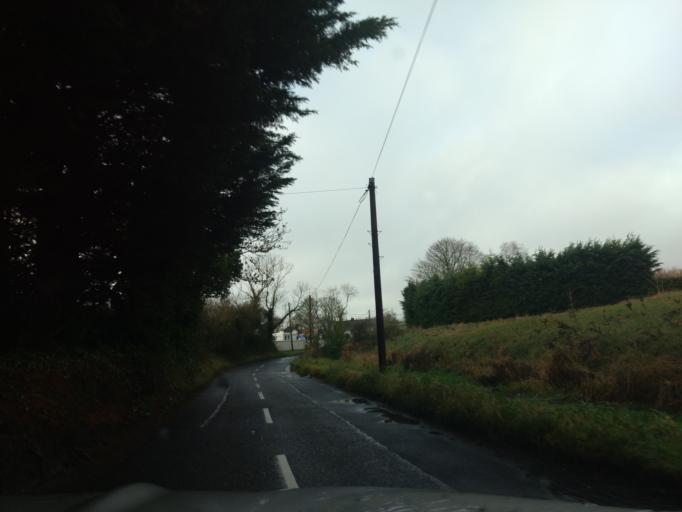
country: IE
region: Leinster
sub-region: Fingal County
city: Swords
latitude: 53.4675
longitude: -6.2087
